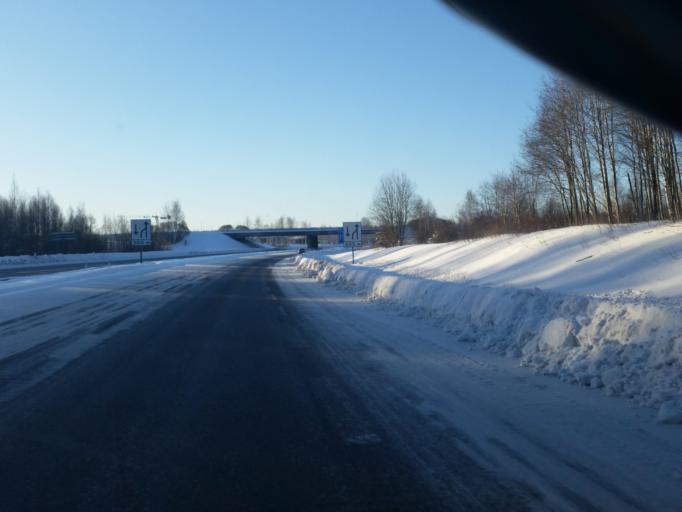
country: SE
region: Norrbotten
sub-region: Pitea Kommun
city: Pitea
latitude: 65.3279
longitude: 21.4397
